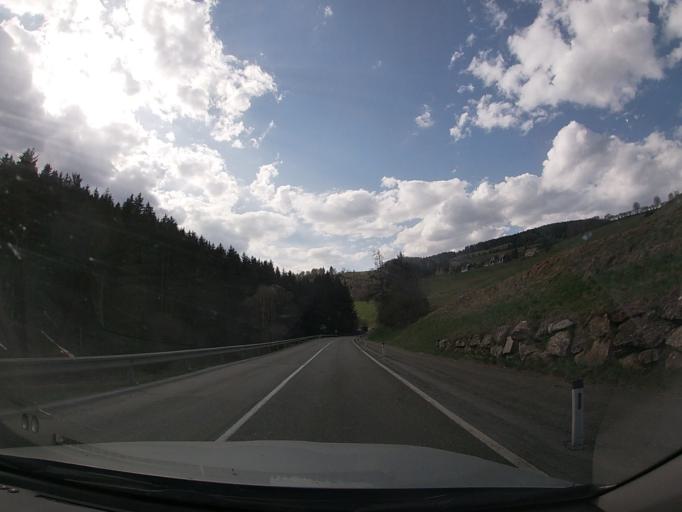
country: AT
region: Styria
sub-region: Politischer Bezirk Murau
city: Perchau am Sattel
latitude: 47.0905
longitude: 14.4367
